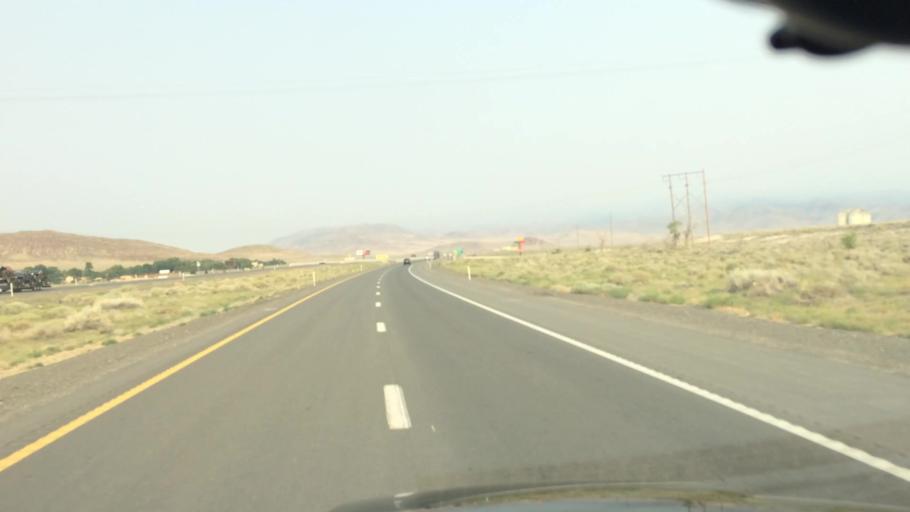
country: US
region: Nevada
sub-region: Lyon County
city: Fernley
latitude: 39.6154
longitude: -119.2561
